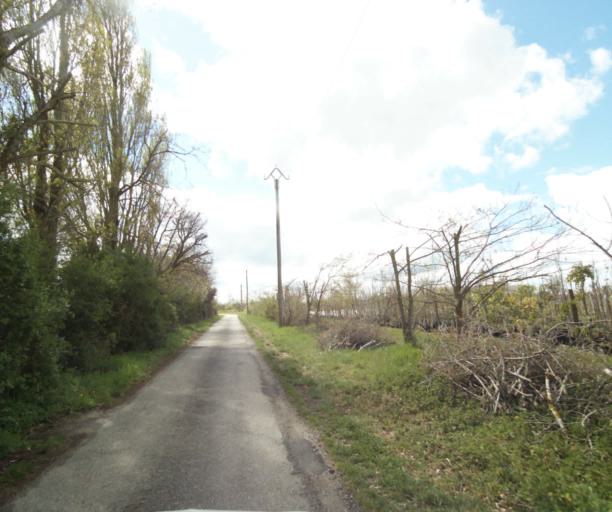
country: FR
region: Midi-Pyrenees
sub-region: Departement de l'Ariege
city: Saverdun
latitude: 43.2600
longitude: 1.5970
